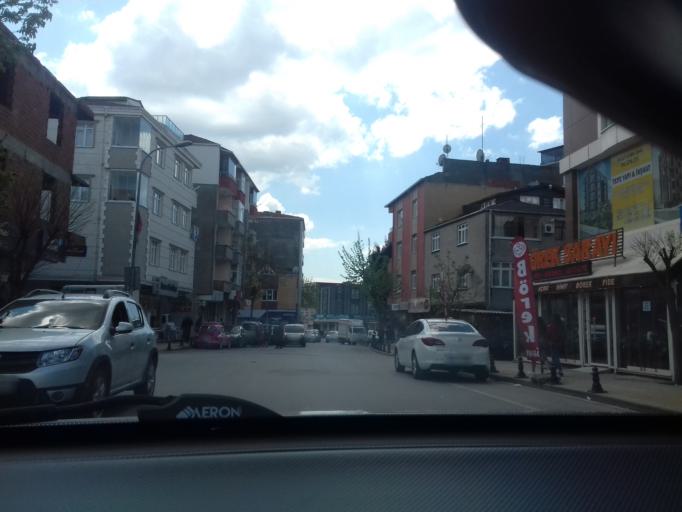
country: TR
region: Istanbul
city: Pendik
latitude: 40.8801
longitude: 29.2868
